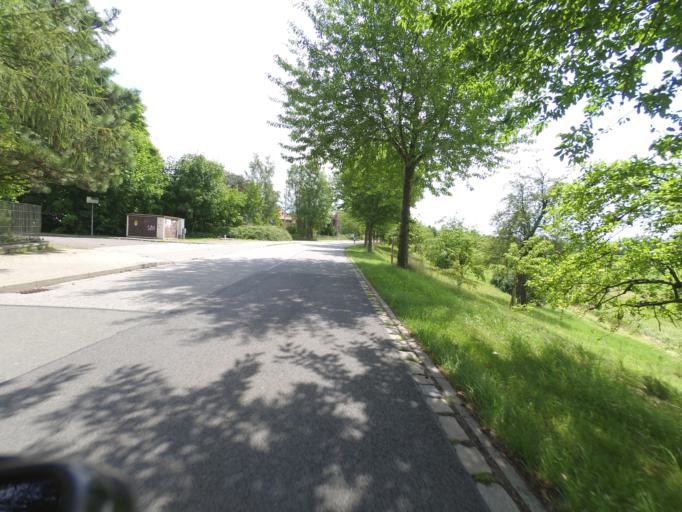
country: DE
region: Saxony
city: Heidenau
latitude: 51.0046
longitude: 13.8768
